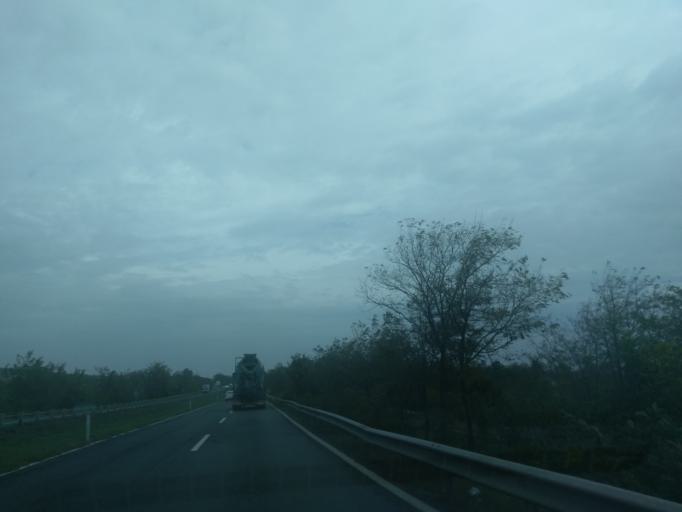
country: TR
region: Istanbul
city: Canta
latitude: 41.0751
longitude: 28.1362
